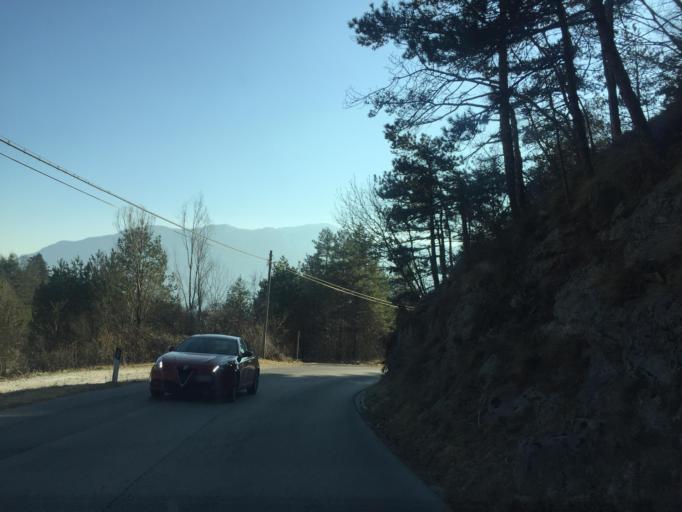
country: IT
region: Friuli Venezia Giulia
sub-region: Provincia di Udine
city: Tolmezzo
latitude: 46.4040
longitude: 13.0396
